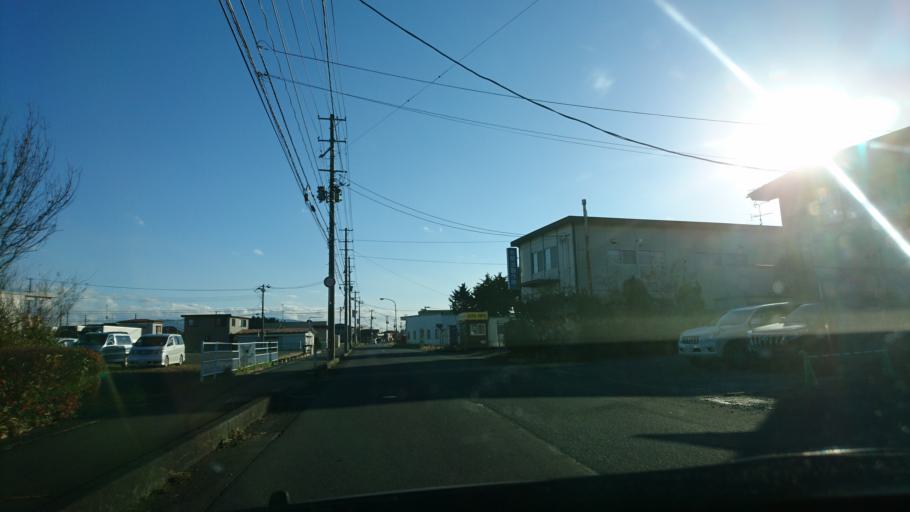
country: JP
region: Iwate
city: Mizusawa
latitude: 39.1172
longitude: 141.1555
